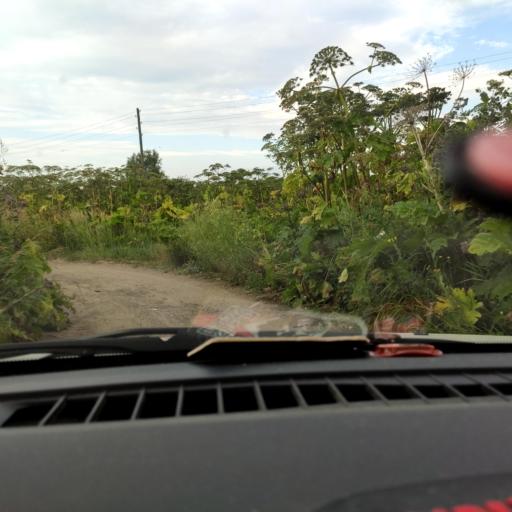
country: RU
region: Perm
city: Kultayevo
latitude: 57.8568
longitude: 55.9686
